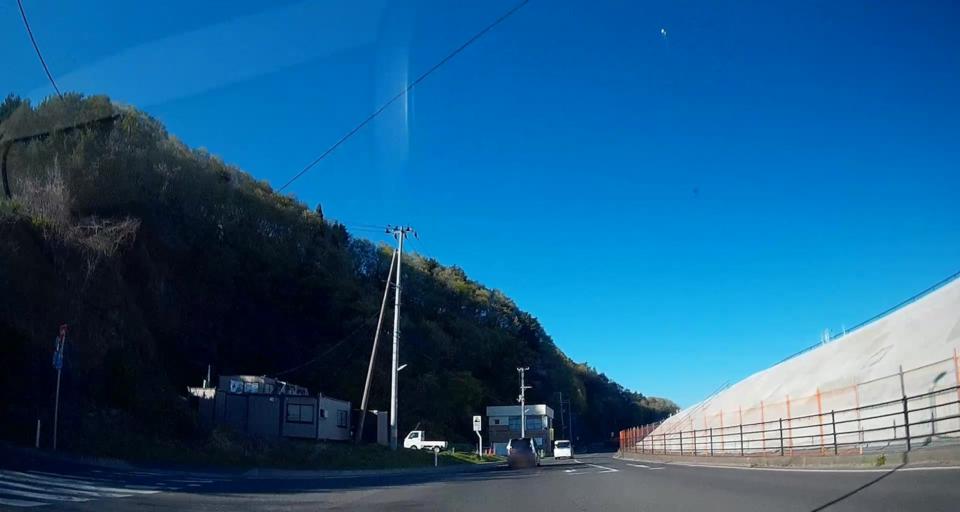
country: JP
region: Iwate
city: Miyako
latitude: 39.6081
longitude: 141.9578
